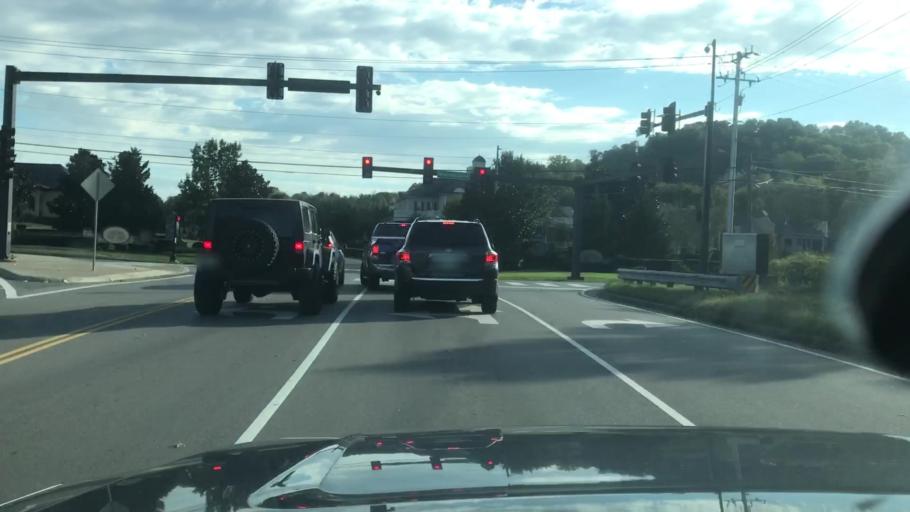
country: US
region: Tennessee
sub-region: Williamson County
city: Brentwood
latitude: 36.0162
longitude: -86.8212
